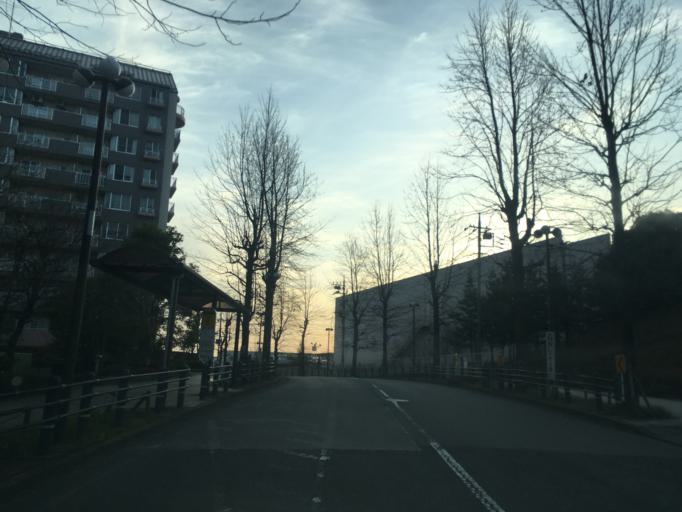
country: JP
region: Tokyo
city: Hino
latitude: 35.6114
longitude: 139.3942
